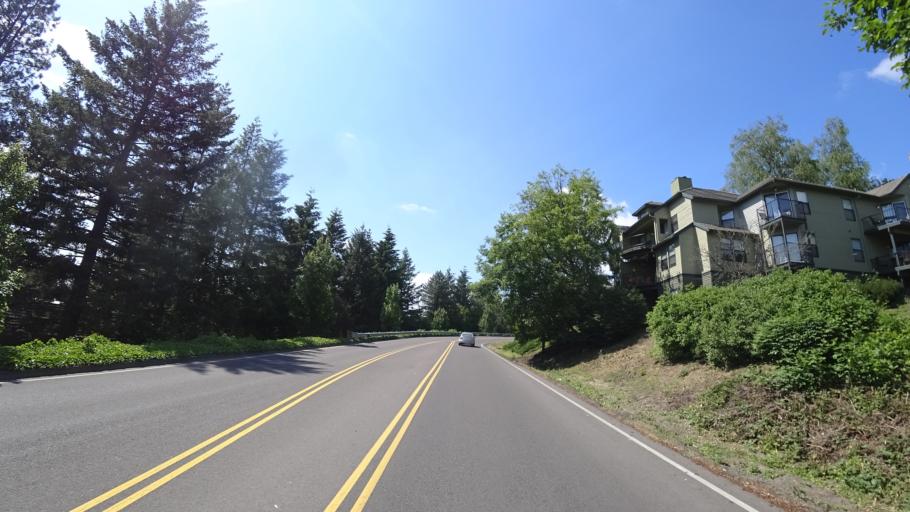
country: US
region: Oregon
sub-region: Washington County
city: Metzger
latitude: 45.4314
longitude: -122.7187
